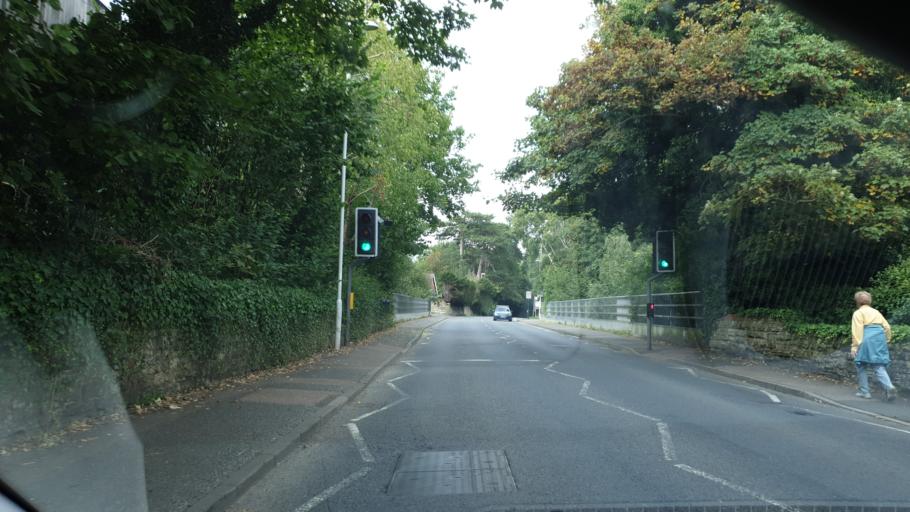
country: GB
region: England
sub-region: West Sussex
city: East Grinstead
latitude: 51.1259
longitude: -0.0036
